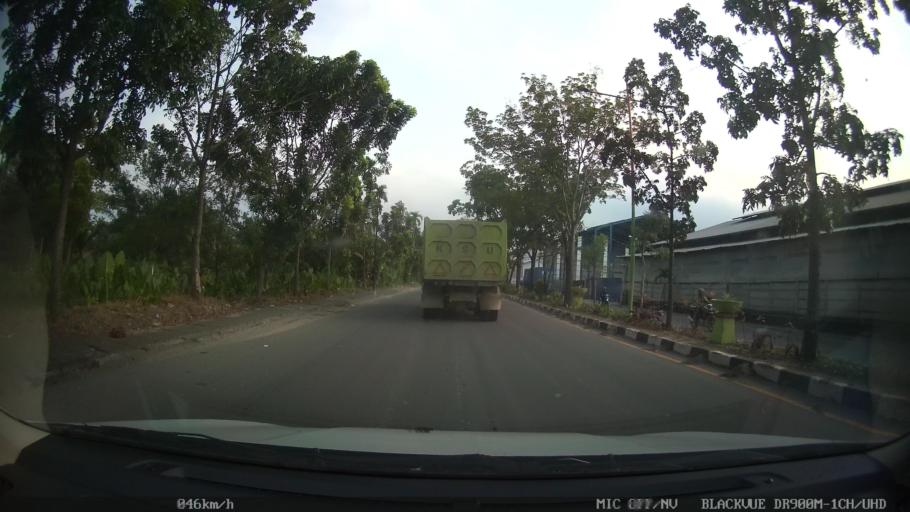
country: ID
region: North Sumatra
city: Binjai
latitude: 3.6064
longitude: 98.5333
